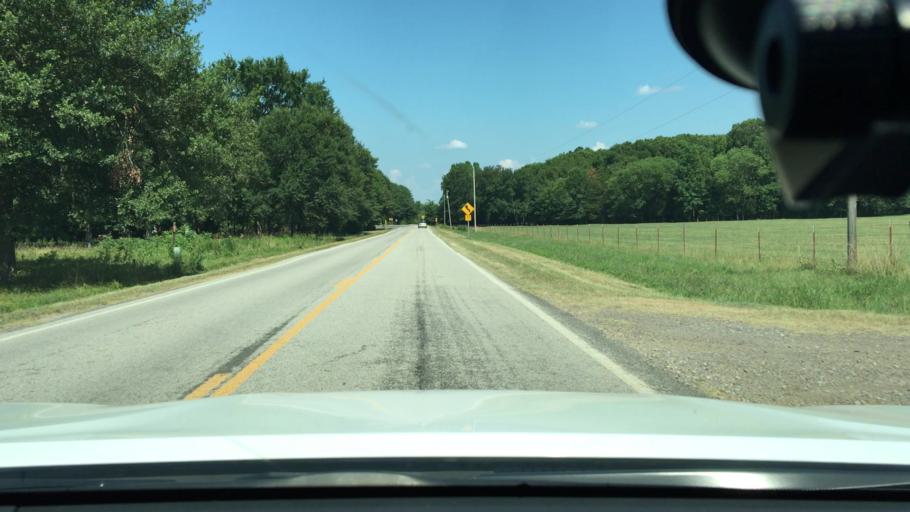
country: US
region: Arkansas
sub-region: Johnson County
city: Clarksville
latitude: 35.3574
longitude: -93.5528
